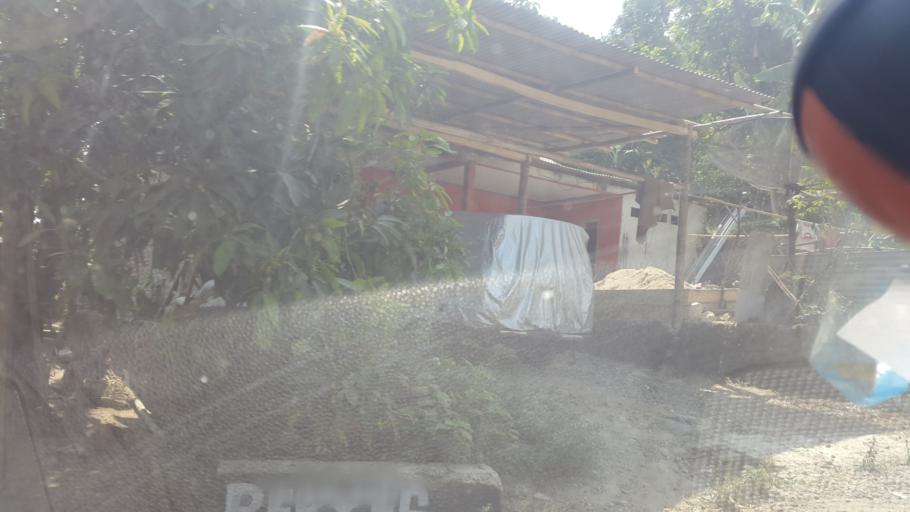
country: ID
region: West Java
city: Sindangsari
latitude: -6.9388
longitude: 106.6565
